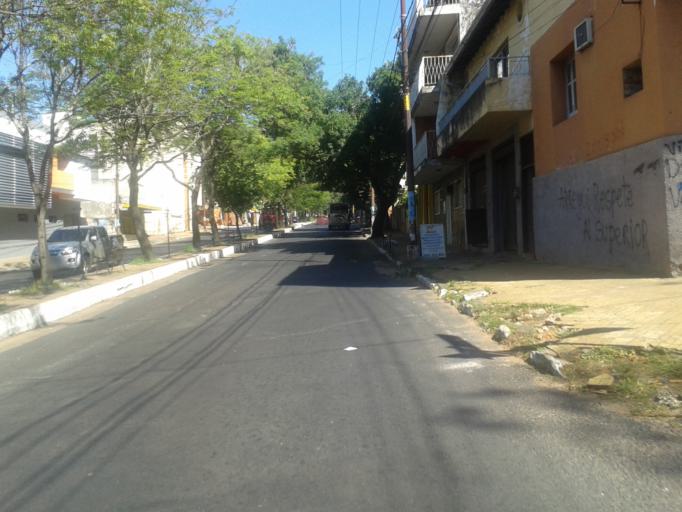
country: PY
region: Asuncion
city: Asuncion
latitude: -25.2918
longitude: -57.6377
